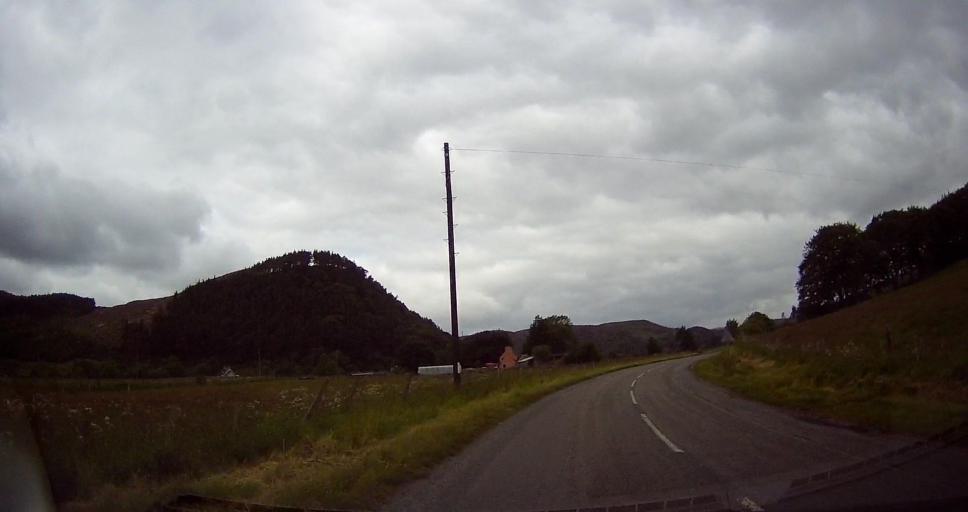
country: GB
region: Scotland
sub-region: Highland
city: Dornoch
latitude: 57.9934
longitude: -4.1704
